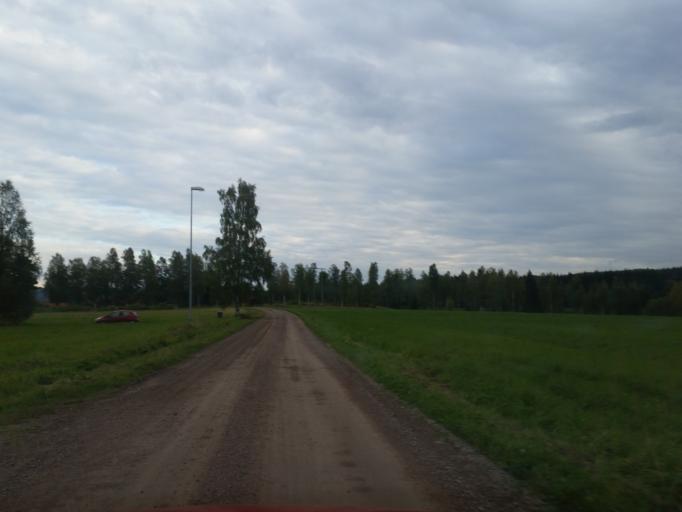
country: SE
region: Dalarna
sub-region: Leksand Municipality
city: Smedby
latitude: 60.6773
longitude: 15.1390
